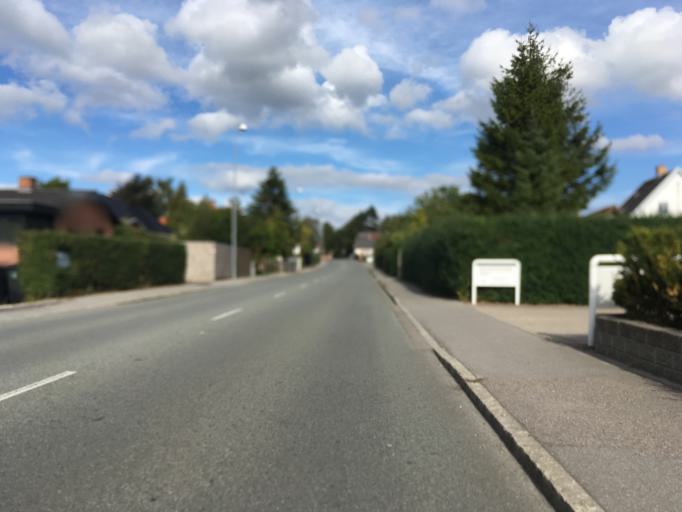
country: DK
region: Capital Region
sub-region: Hillerod Kommune
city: Hillerod
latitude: 55.9338
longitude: 12.2875
